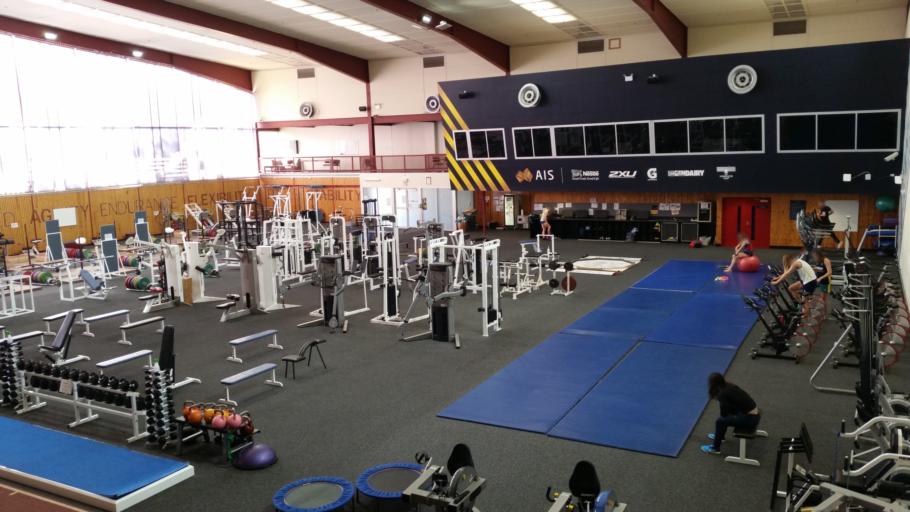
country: AU
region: Australian Capital Territory
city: Kaleen
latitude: -35.2467
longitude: 149.1028
